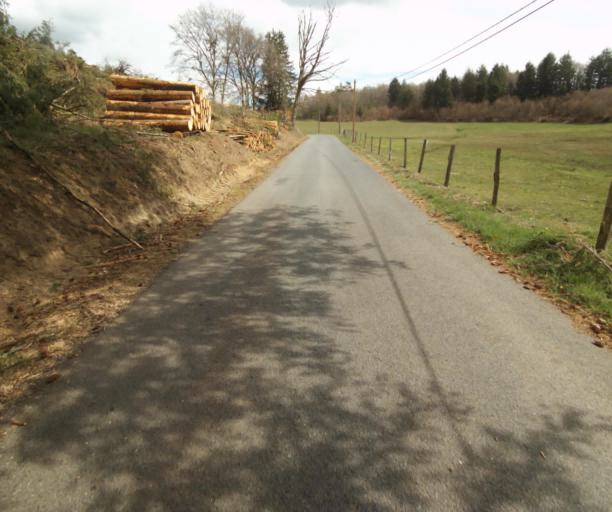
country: FR
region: Limousin
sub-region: Departement de la Correze
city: Correze
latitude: 45.3834
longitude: 1.9556
